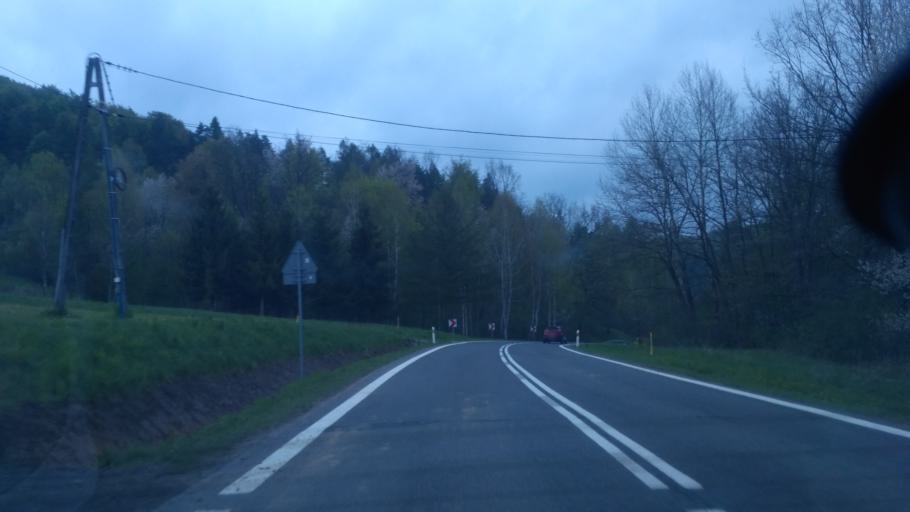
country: PL
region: Subcarpathian Voivodeship
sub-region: Powiat sanocki
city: Zagorz
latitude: 49.5347
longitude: 22.2990
